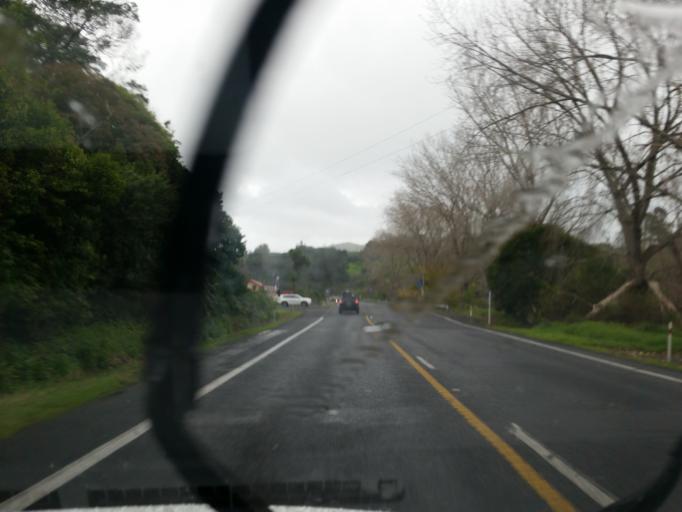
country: NZ
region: Waikato
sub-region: Hauraki District
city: Waihi
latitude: -37.4125
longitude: 175.7782
